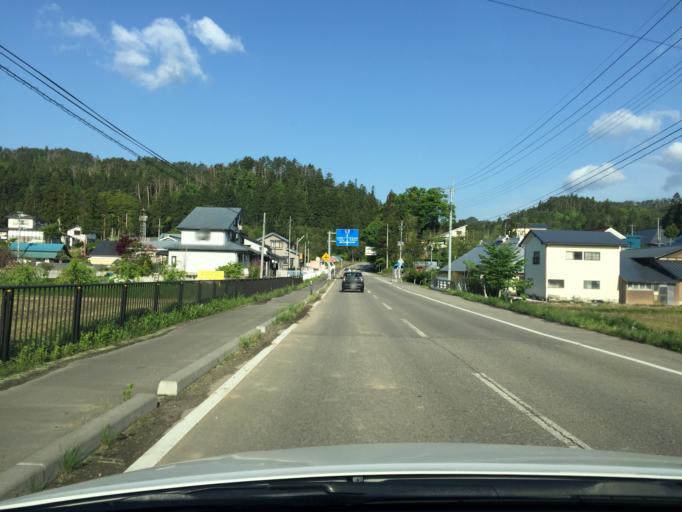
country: JP
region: Fukushima
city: Kitakata
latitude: 37.6664
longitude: 139.8478
